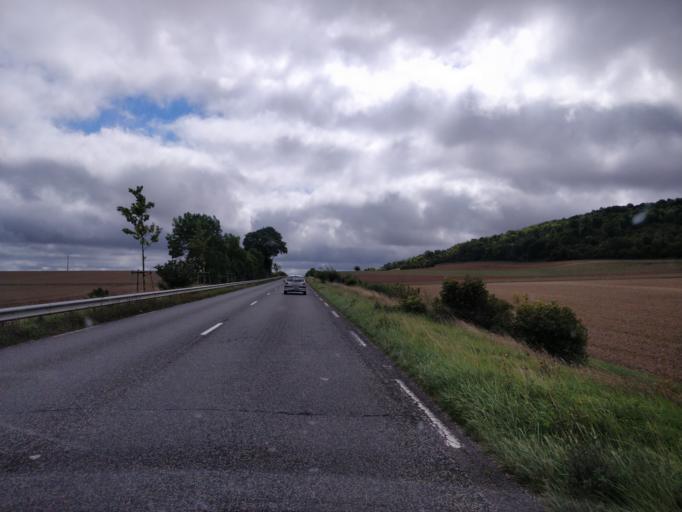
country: FR
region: Champagne-Ardenne
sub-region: Departement de l'Aube
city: Bouilly
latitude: 48.1815
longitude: 4.0106
